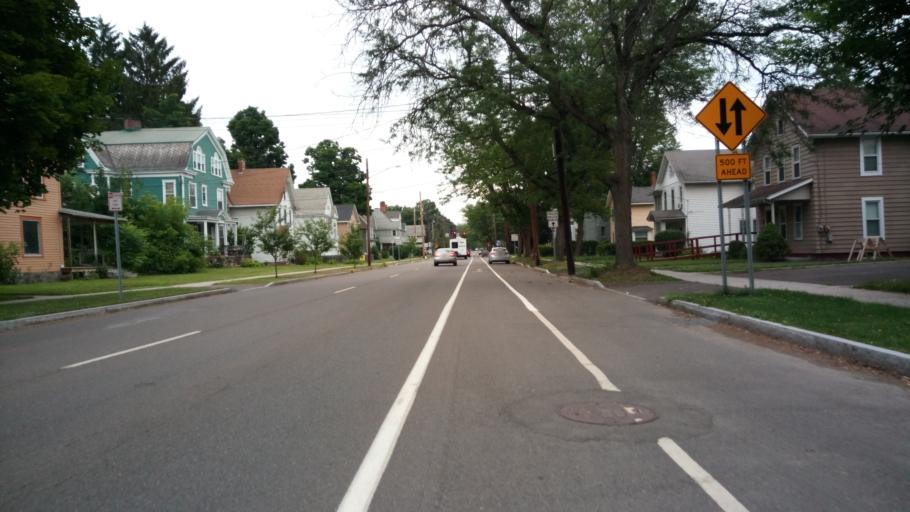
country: US
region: New York
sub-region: Chemung County
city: Elmira
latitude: 42.0830
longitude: -76.8237
